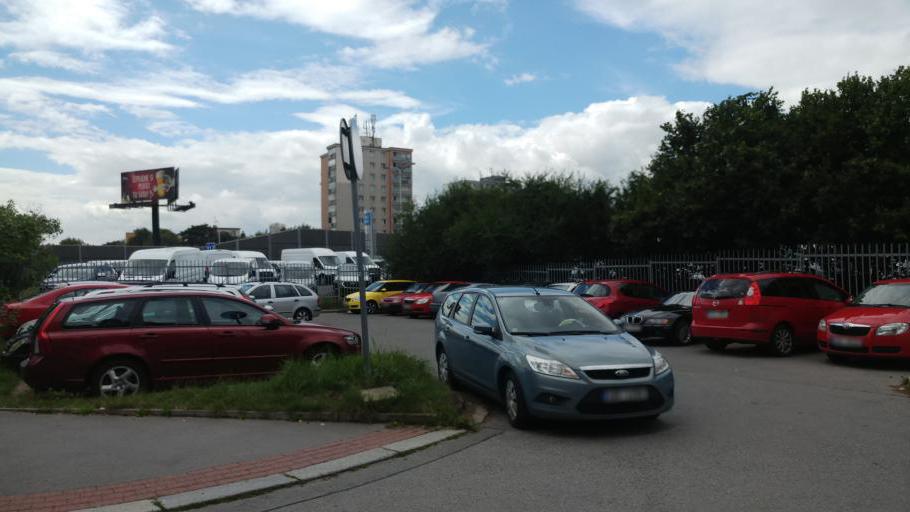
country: CZ
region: Praha
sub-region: Praha 8
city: Karlin
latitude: 50.0493
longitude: 14.4821
